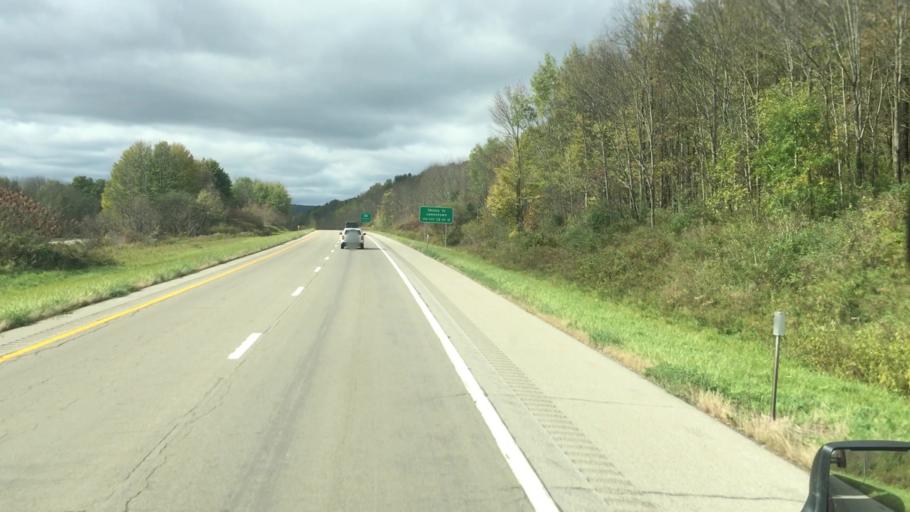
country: US
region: New York
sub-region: Chautauqua County
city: Falconer
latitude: 42.1380
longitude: -79.1625
